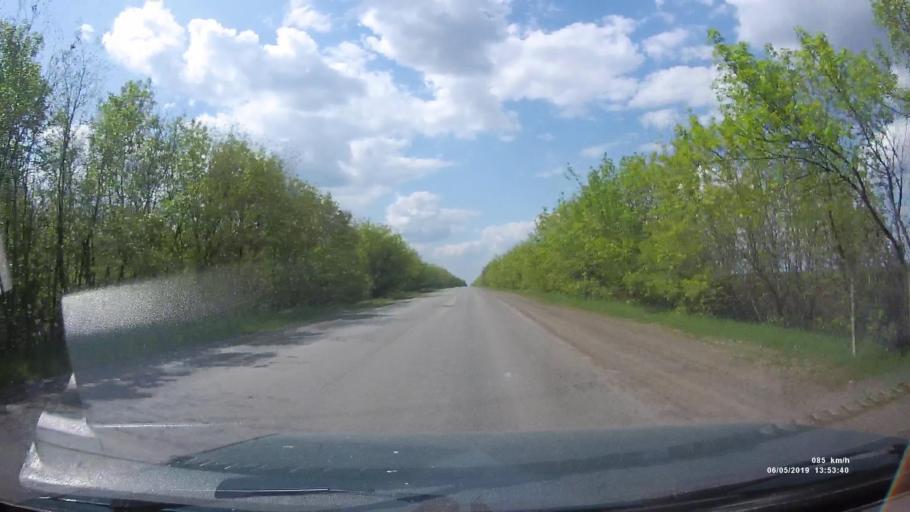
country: RU
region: Rostov
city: Melikhovskaya
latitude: 47.6696
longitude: 40.4589
